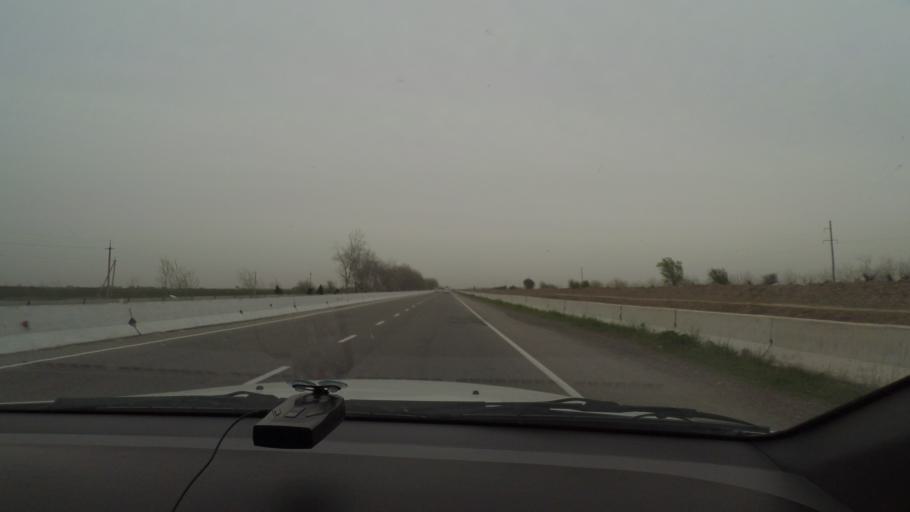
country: UZ
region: Jizzax
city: Dustlik
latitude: 40.4075
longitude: 68.1981
